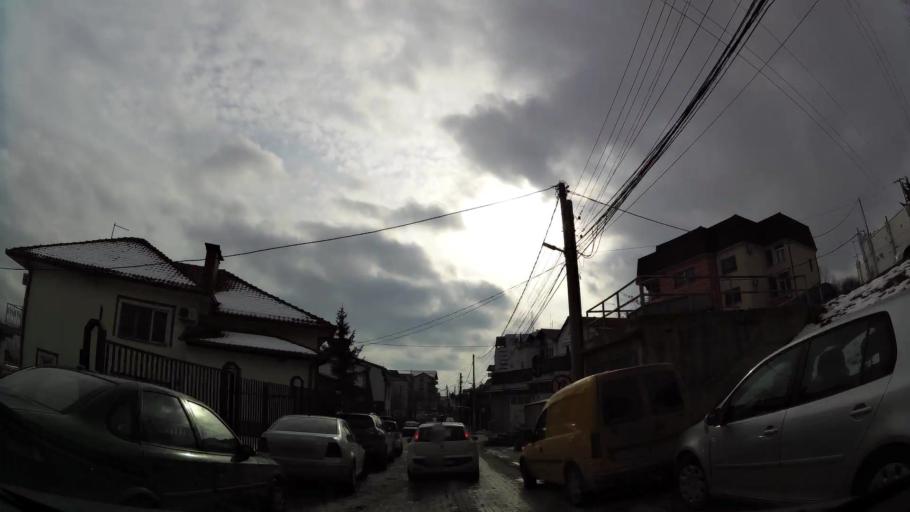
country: XK
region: Pristina
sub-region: Komuna e Prishtines
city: Pristina
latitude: 42.6650
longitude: 21.1520
